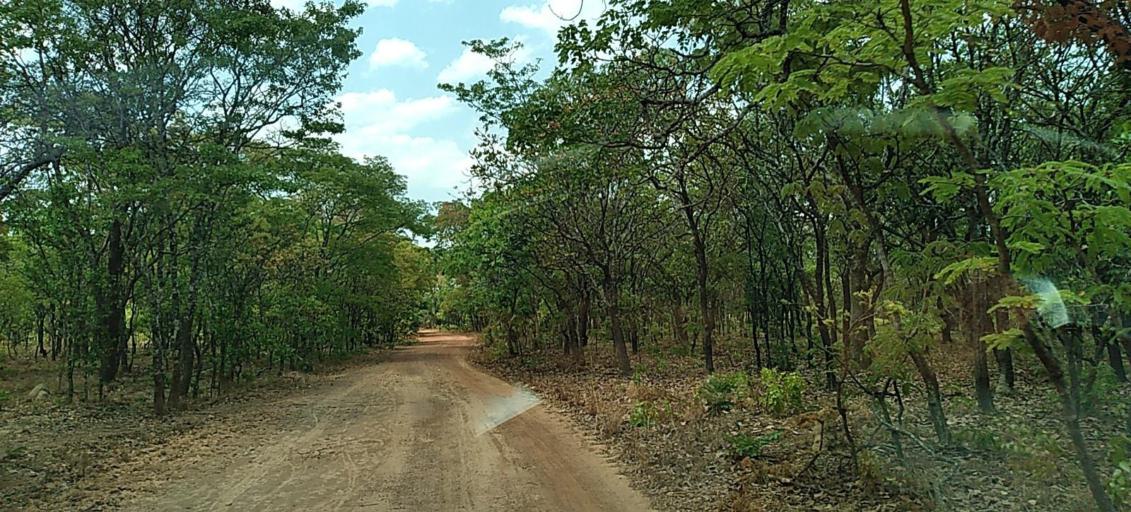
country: ZM
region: Copperbelt
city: Chililabombwe
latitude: -12.5076
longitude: 27.6332
